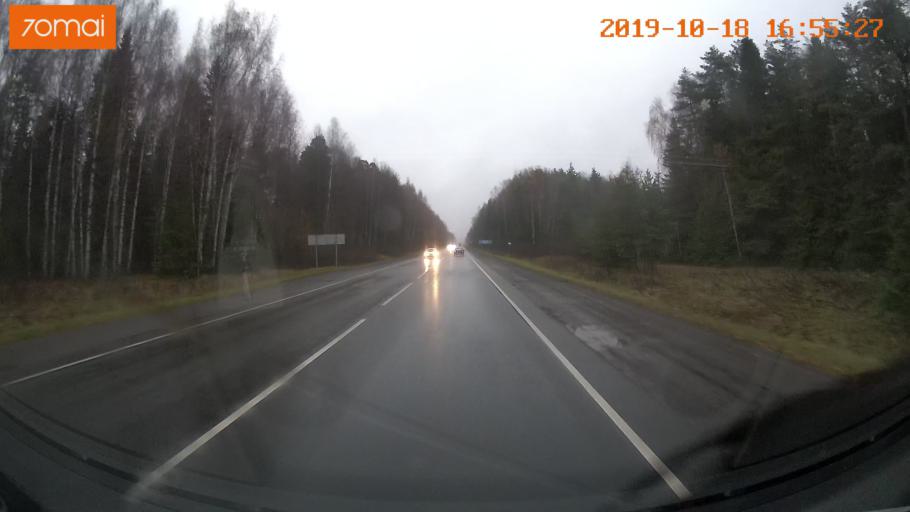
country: RU
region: Ivanovo
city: Novoye Leushino
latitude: 56.6441
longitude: 40.5794
